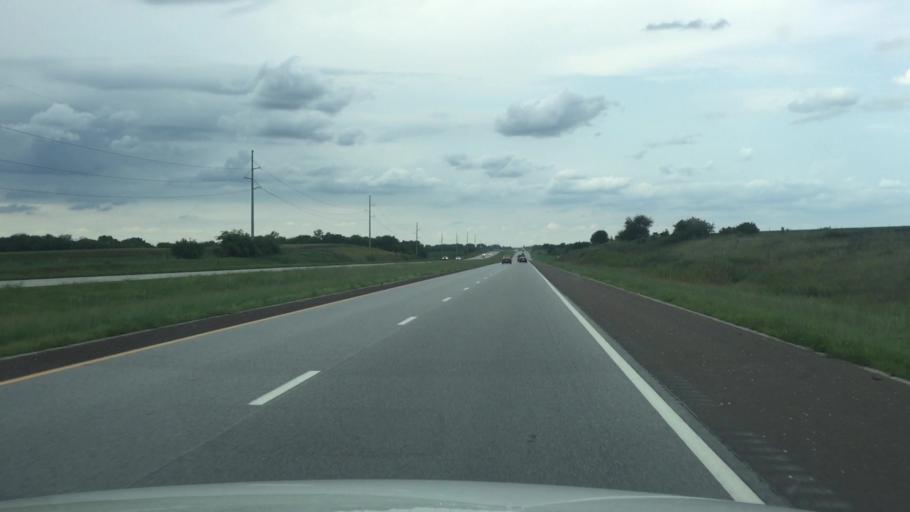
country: US
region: Kansas
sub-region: Miami County
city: Louisburg
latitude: 38.6999
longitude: -94.6763
